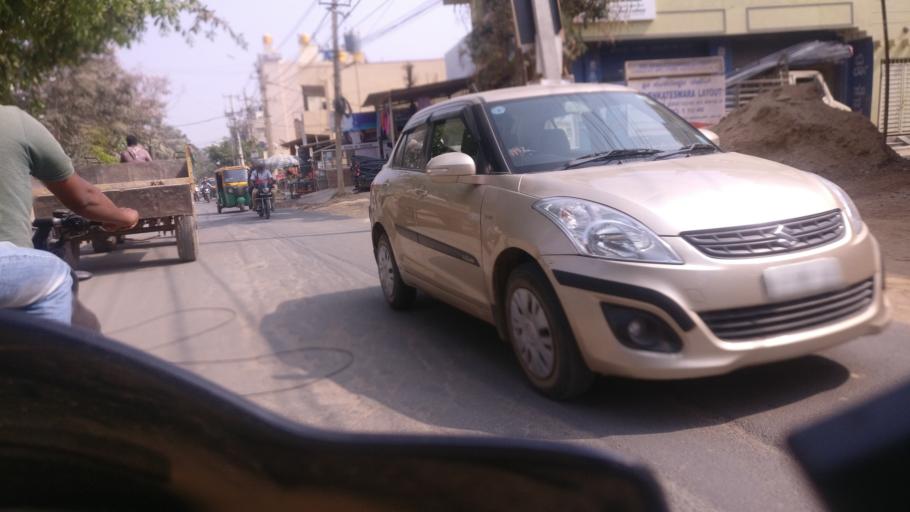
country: IN
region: Karnataka
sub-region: Bangalore Urban
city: Bangalore
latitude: 12.8825
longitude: 77.6723
